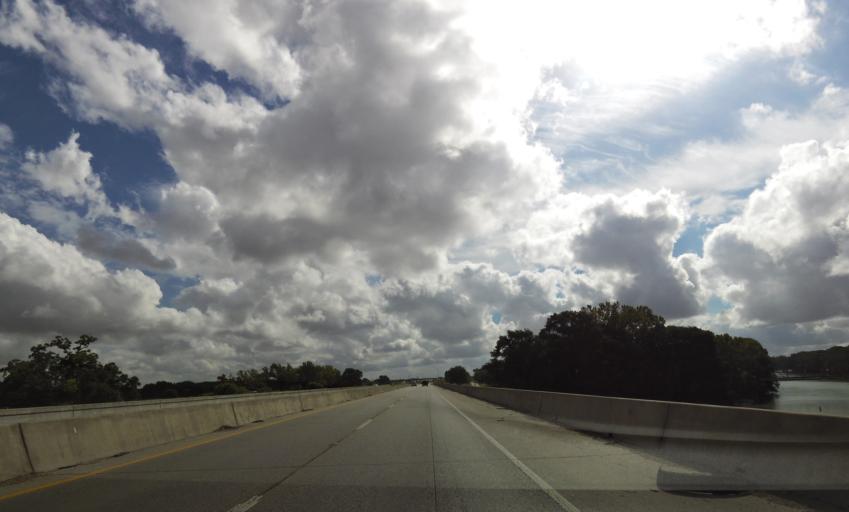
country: US
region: Texas
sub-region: Guadalupe County
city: McQueeney
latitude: 29.5663
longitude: -98.0237
